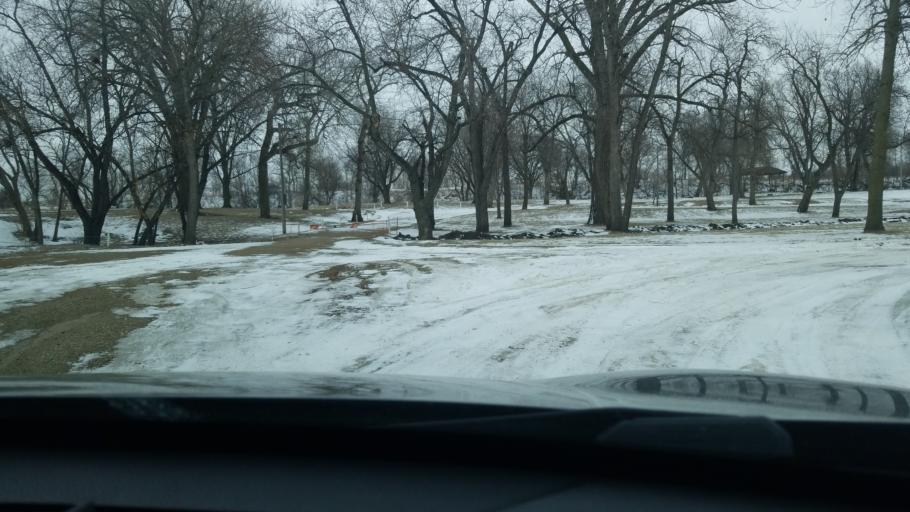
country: US
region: Iowa
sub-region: Lyon County
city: Rock Rapids
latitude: 43.4364
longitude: -96.1673
